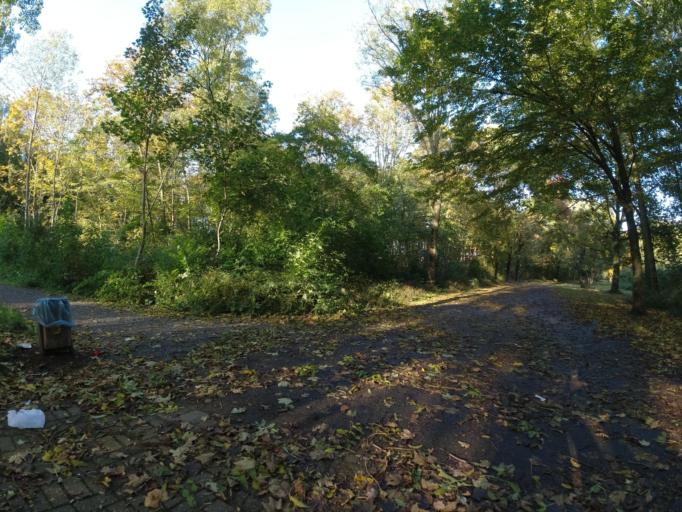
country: DE
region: North Rhine-Westphalia
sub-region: Regierungsbezirk Dusseldorf
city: Moers
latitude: 51.4092
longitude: 6.6698
